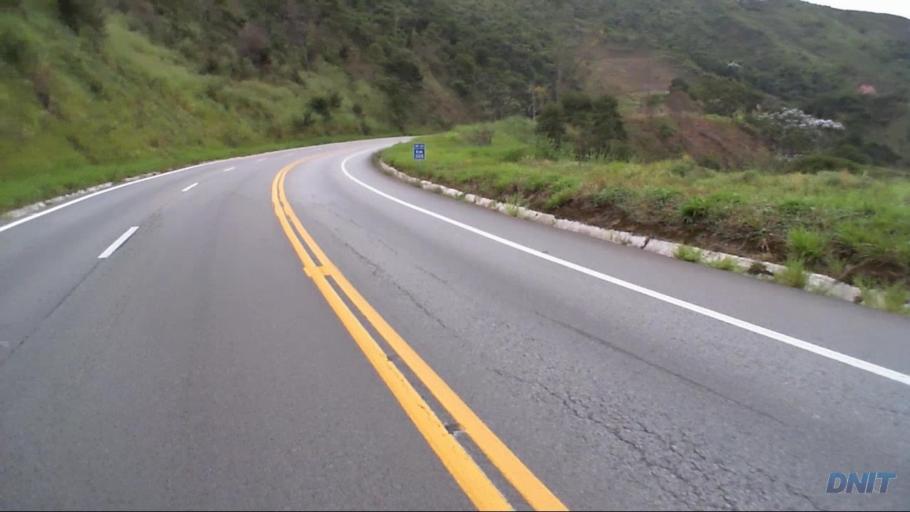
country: BR
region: Minas Gerais
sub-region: Nova Era
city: Nova Era
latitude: -19.6352
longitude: -42.8994
